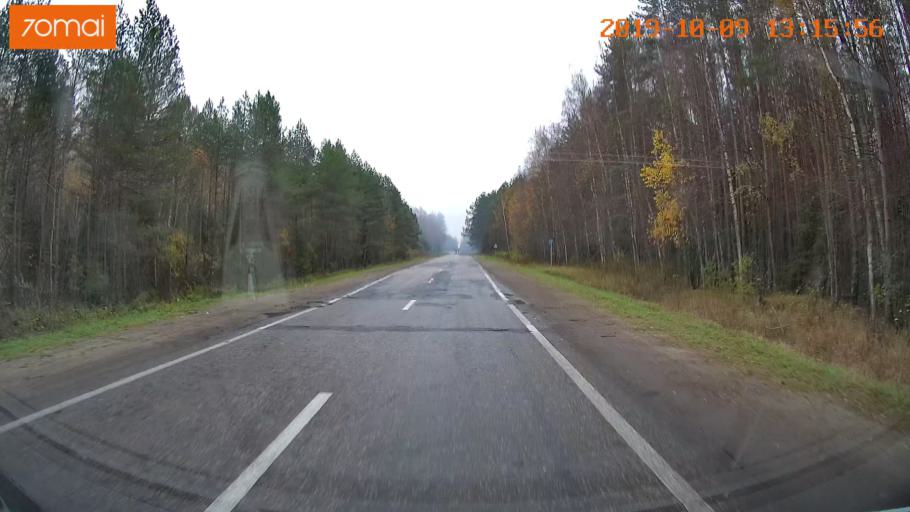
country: RU
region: Jaroslavl
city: Lyubim
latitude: 58.3645
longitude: 40.7592
